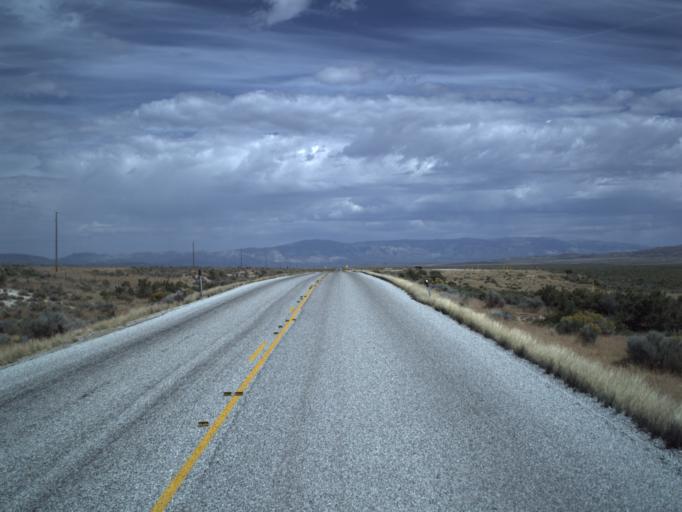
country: US
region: Utah
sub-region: Tooele County
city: Wendover
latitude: 41.5597
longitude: -113.5836
